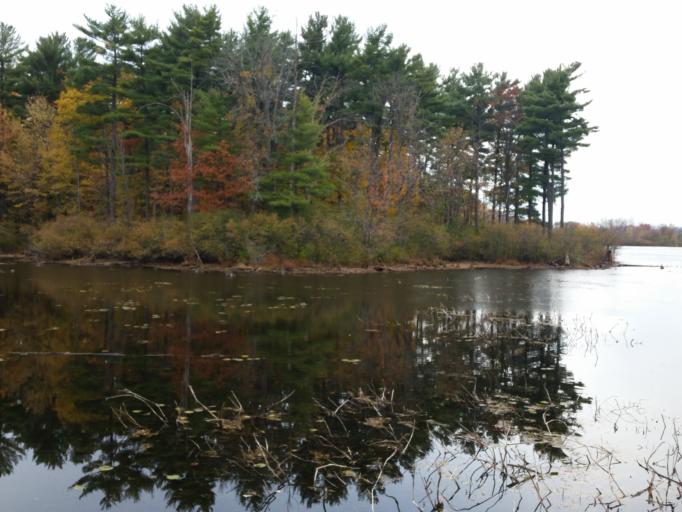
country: CA
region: Ontario
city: Bells Corners
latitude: 45.3686
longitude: -75.7943
